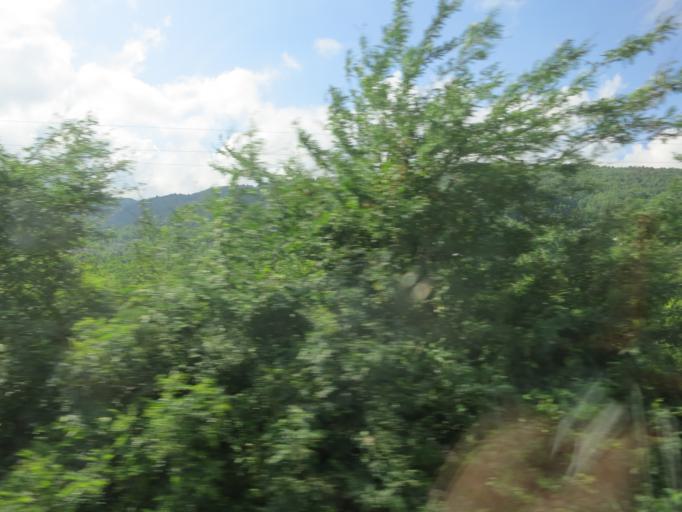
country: GE
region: Imereti
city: Samtredia
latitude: 42.1081
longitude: 42.3202
